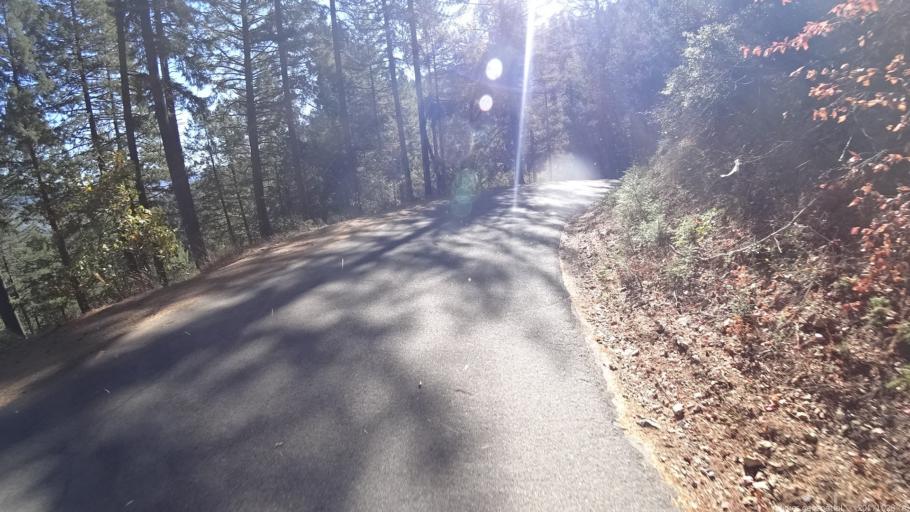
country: US
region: California
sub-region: Trinity County
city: Lewiston
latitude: 40.8144
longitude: -122.6487
